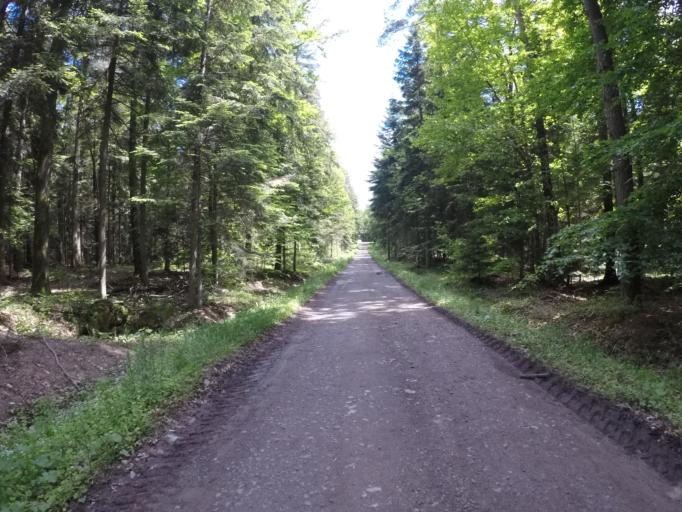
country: PL
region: Swietokrzyskie
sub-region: Powiat kielecki
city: Kostomloty Pierwsze
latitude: 50.9182
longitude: 20.6387
